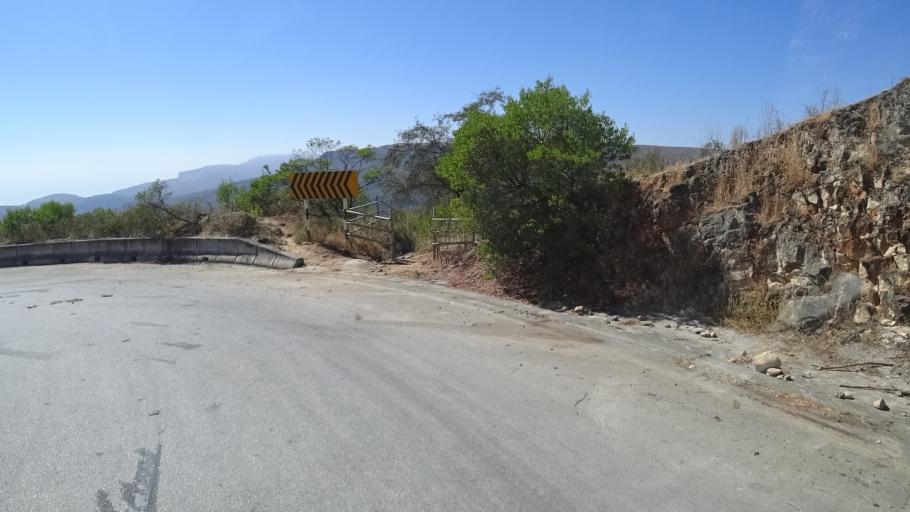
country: YE
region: Al Mahrah
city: Hawf
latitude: 16.7669
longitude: 53.3366
